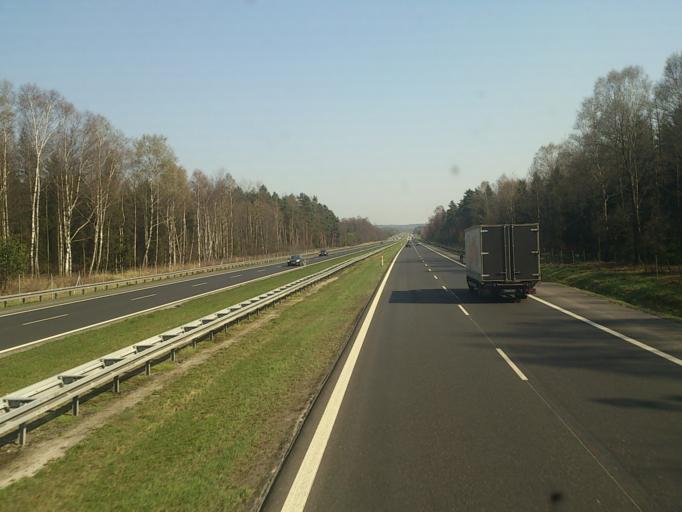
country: PL
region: Lesser Poland Voivodeship
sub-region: Powiat chrzanowski
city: Bolecin
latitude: 50.1324
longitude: 19.4766
